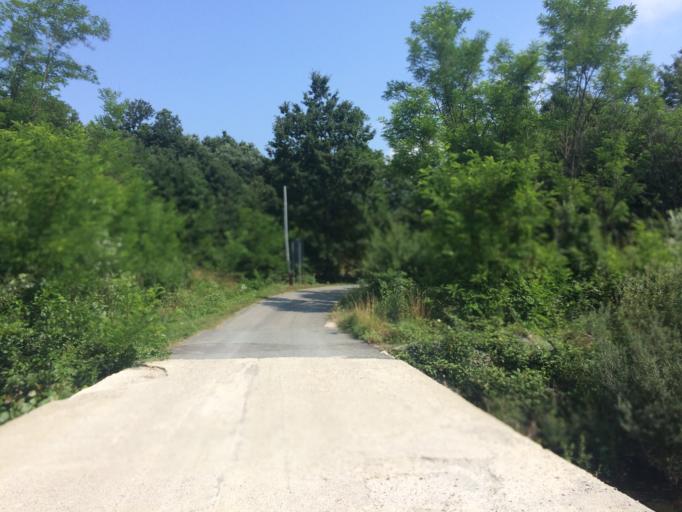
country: IT
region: Piedmont
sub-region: Provincia di Alessandria
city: Pareto
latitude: 44.4900
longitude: 8.3505
